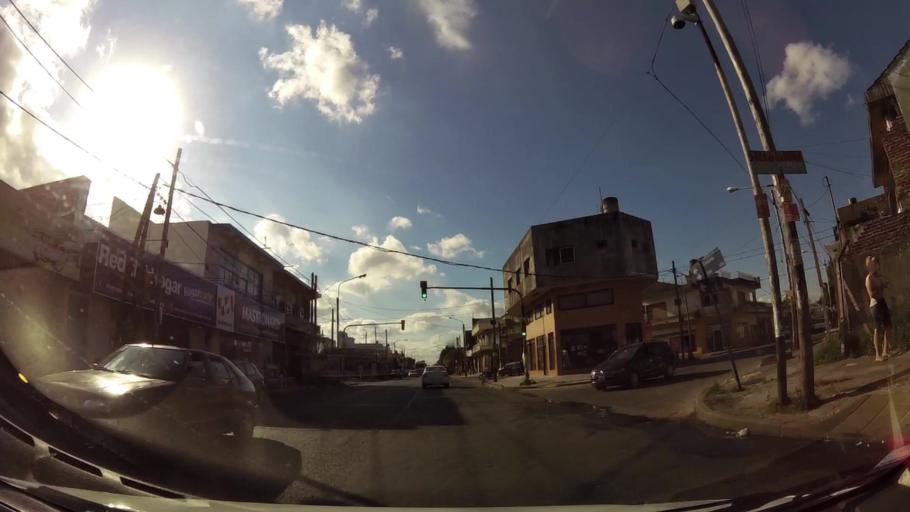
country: AR
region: Buenos Aires
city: San Justo
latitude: -34.7027
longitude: -58.5946
